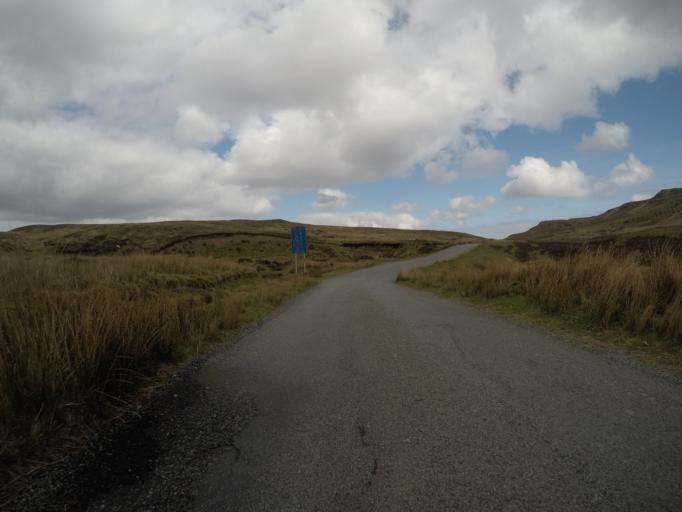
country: GB
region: Scotland
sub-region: Highland
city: Isle of Skye
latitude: 57.3839
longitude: -6.3564
